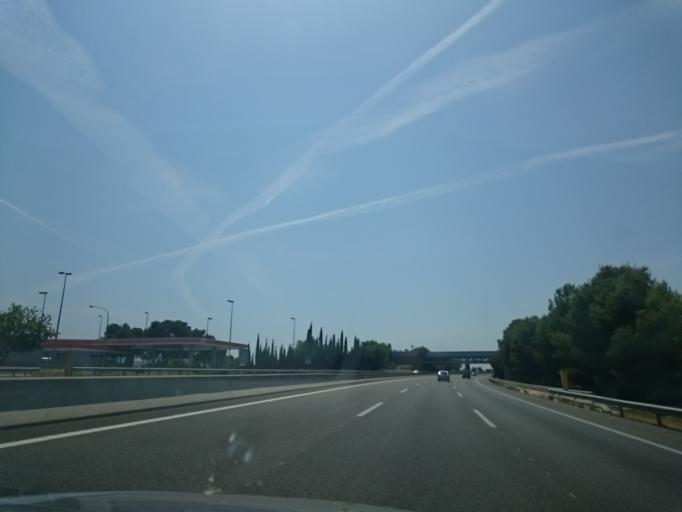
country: ES
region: Catalonia
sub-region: Provincia de Tarragona
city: Sant Jaume dels Domenys
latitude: 41.2901
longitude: 1.5942
